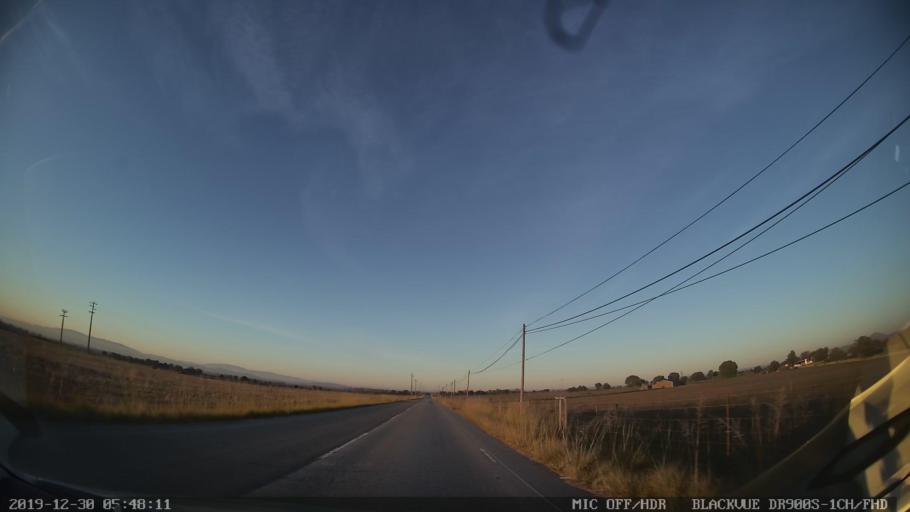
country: PT
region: Castelo Branco
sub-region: Idanha-A-Nova
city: Idanha-a-Nova
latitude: 39.9595
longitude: -7.2419
